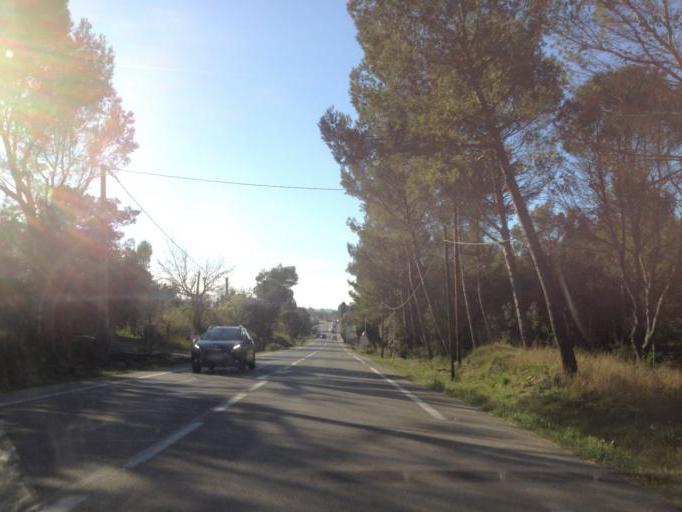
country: FR
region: Provence-Alpes-Cote d'Azur
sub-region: Departement des Bouches-du-Rhone
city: Saint-Cannat
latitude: 43.6100
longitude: 5.3288
